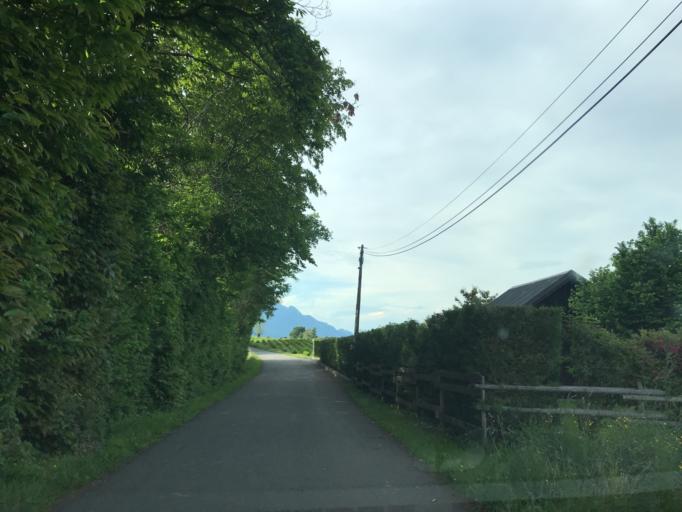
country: FR
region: Rhone-Alpes
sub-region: Departement de la Savoie
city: Vimines
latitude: 45.5577
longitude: 5.8593
